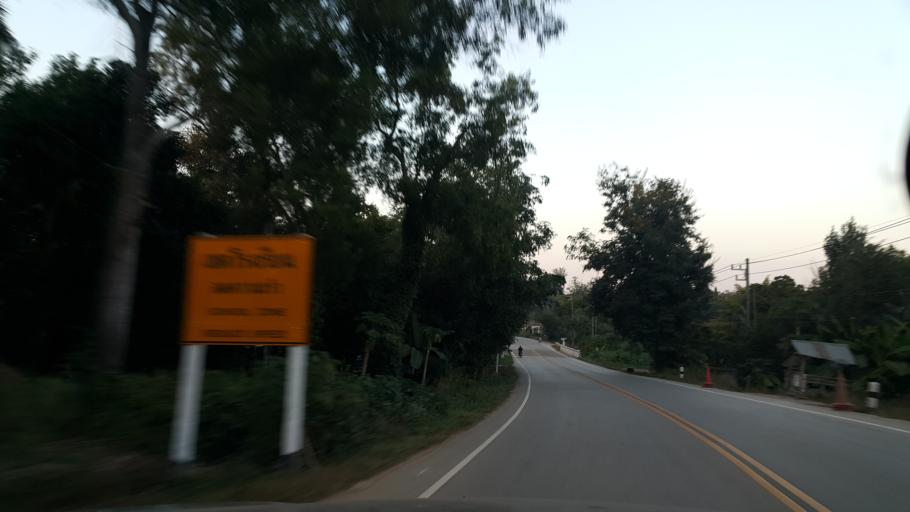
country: TH
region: Phrae
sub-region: Amphoe Wang Chin
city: Wang Chin
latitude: 17.8759
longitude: 99.6194
